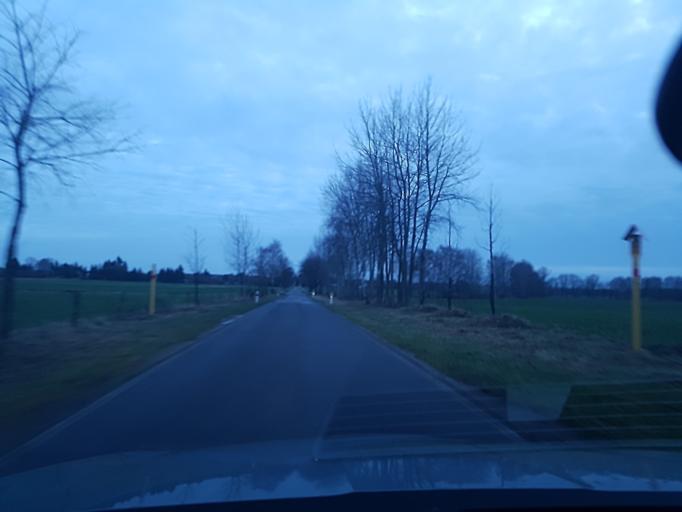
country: DE
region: Brandenburg
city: Finsterwalde
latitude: 51.6105
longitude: 13.6706
